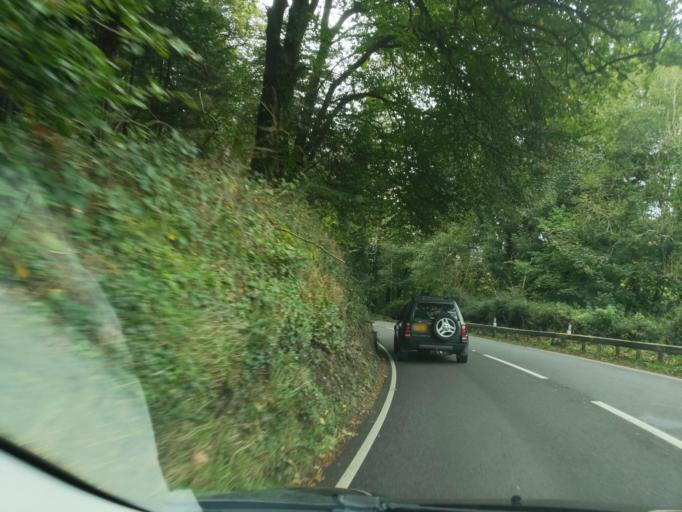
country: GB
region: England
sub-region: Cornwall
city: Wadebridge
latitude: 50.5077
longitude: -4.7827
